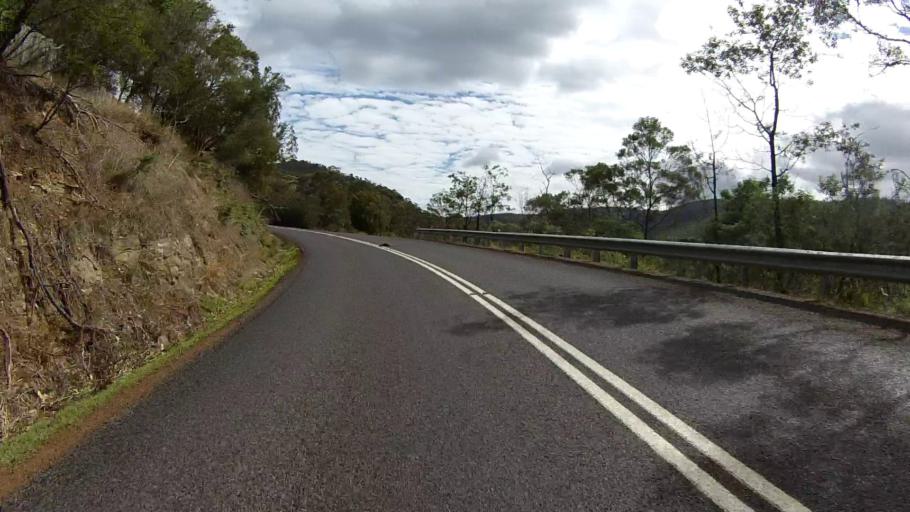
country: AU
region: Tasmania
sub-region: Clarence
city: Lindisfarne
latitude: -42.8063
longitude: 147.3543
